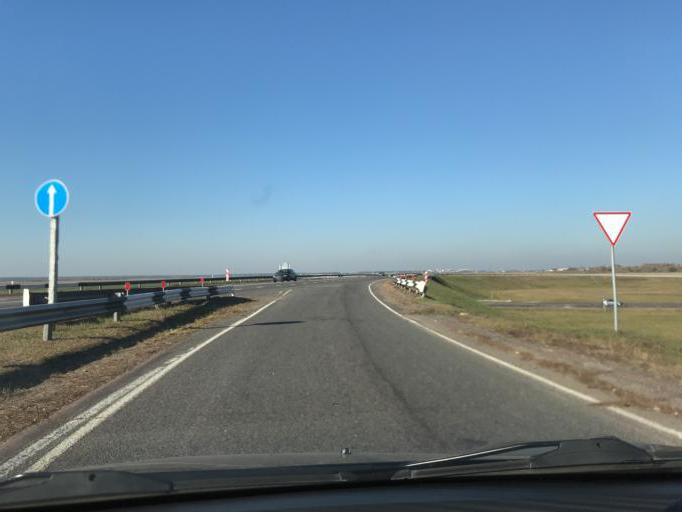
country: BY
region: Gomel
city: Horad Rechytsa
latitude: 52.2904
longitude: 30.4674
